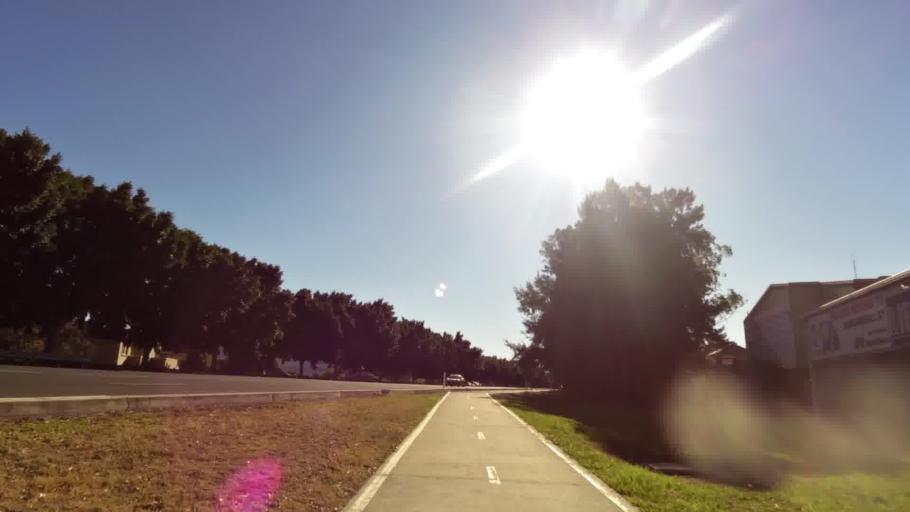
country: AU
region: New South Wales
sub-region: Wollongong
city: Koonawarra
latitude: -34.4890
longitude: 150.7976
